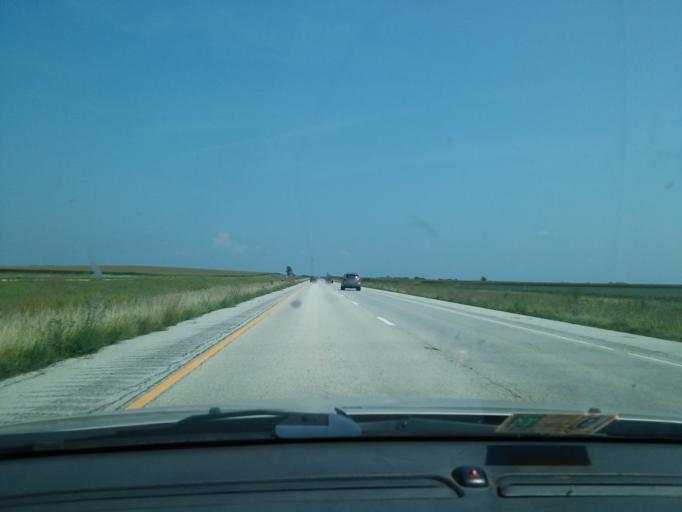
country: US
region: Illinois
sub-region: Morgan County
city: Jacksonville
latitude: 39.7381
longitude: -90.1065
